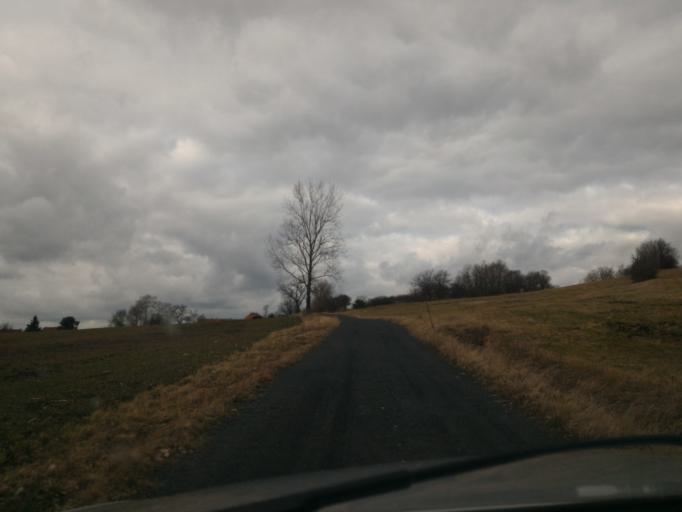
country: CZ
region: Ustecky
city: Varnsdorf
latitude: 50.8925
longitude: 14.6380
